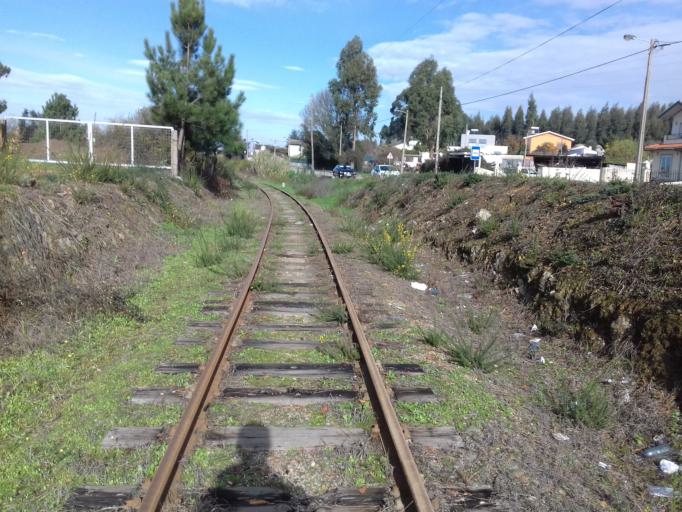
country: PT
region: Aveiro
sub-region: Albergaria-A-Velha
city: Branca
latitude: 40.7686
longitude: -8.4831
